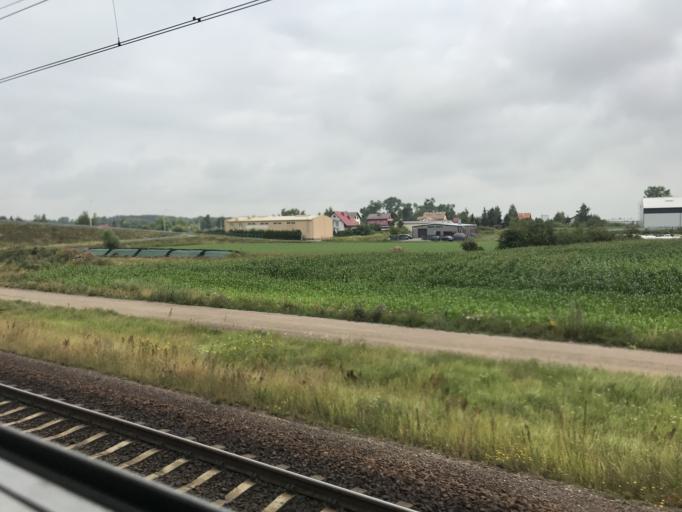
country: PL
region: Pomeranian Voivodeship
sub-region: Powiat gdanski
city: Legowo
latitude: 54.2298
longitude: 18.6482
